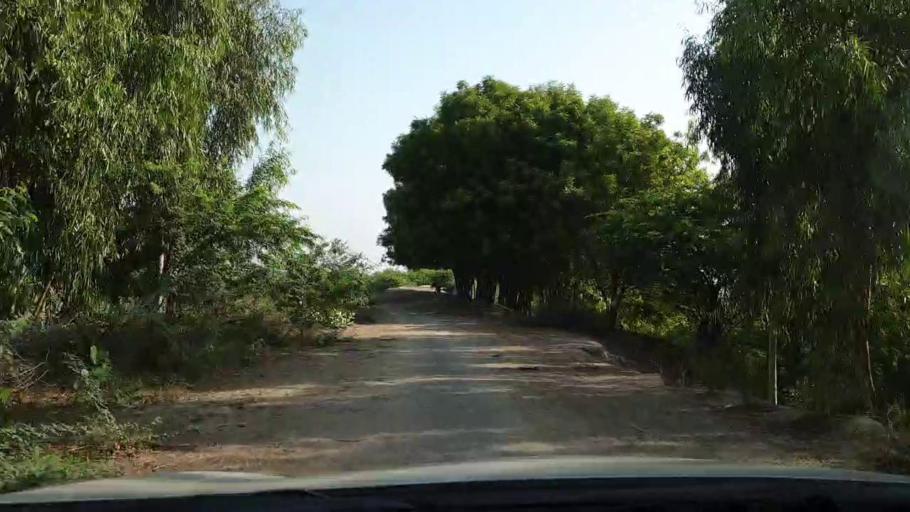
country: PK
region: Sindh
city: Larkana
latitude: 27.5597
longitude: 68.2577
